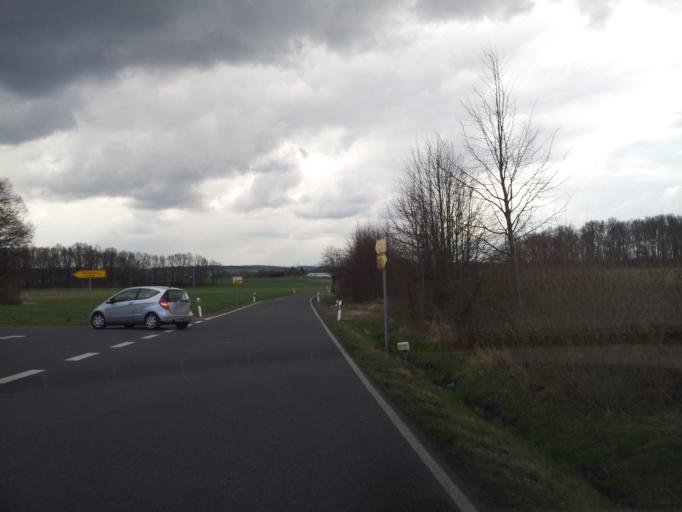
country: DE
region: Saxony
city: Panschwitz-Kuckau
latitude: 51.2564
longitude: 14.2024
